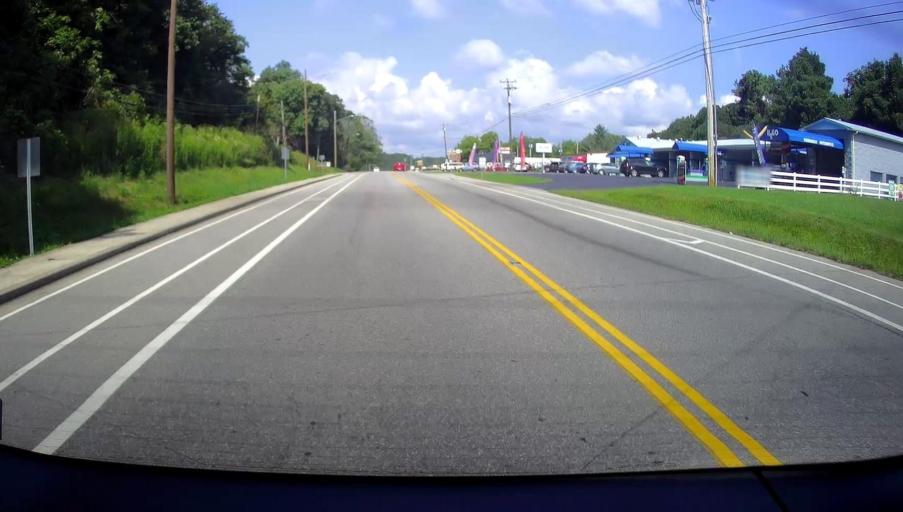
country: US
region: Tennessee
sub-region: Coffee County
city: Manchester
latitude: 35.4904
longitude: -86.0960
